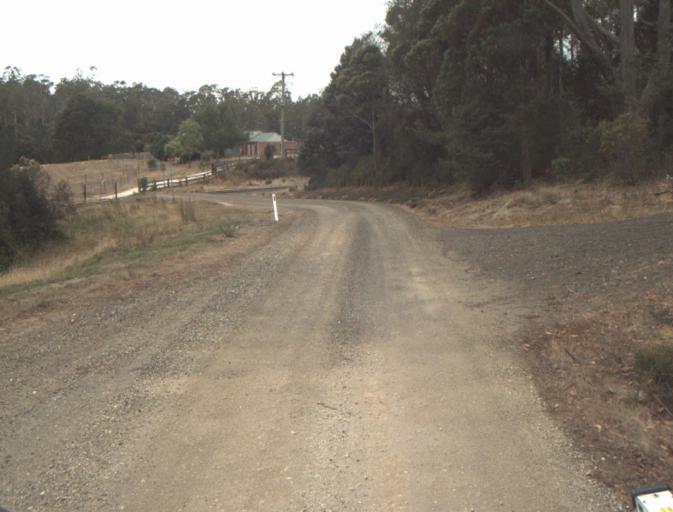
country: AU
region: Tasmania
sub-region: Dorset
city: Bridport
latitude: -41.1766
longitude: 147.2650
